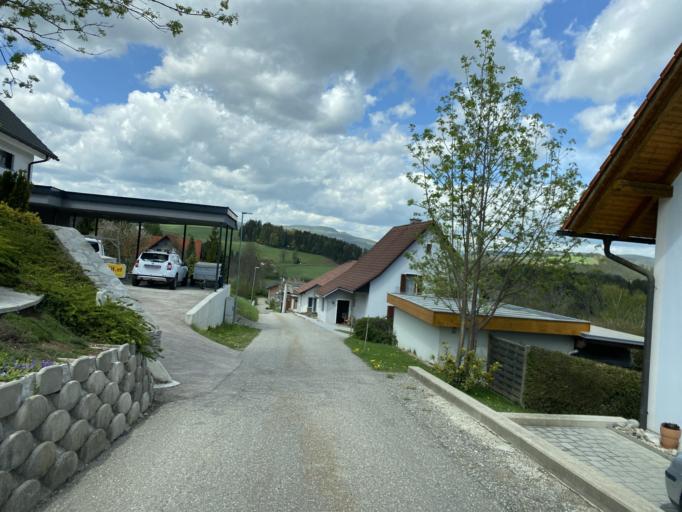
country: AT
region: Styria
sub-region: Politischer Bezirk Weiz
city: Birkfeld
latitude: 47.3550
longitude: 15.6901
